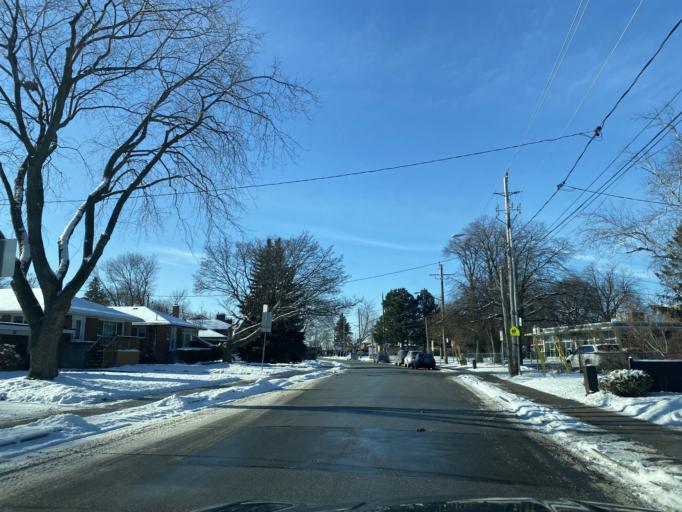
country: CA
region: Ontario
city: Scarborough
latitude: 43.7742
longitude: -79.3073
